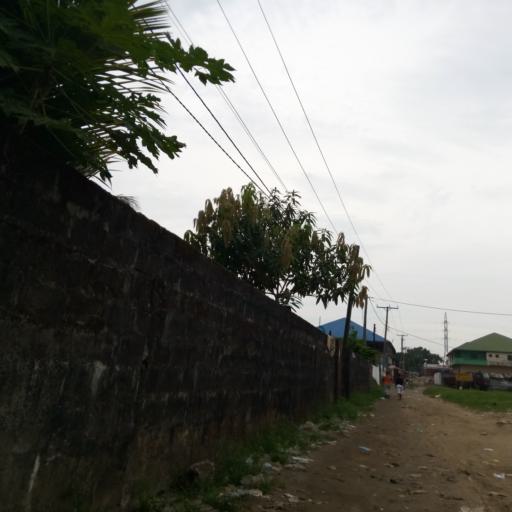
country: LR
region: Montserrado
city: Monrovia
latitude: 6.2942
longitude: -10.6845
